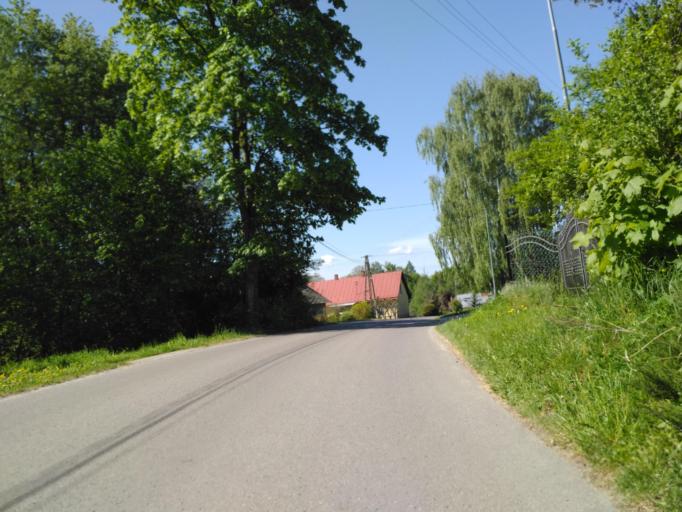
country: PL
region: Subcarpathian Voivodeship
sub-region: Powiat krosnienski
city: Korczyna
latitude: 49.7254
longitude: 21.8294
